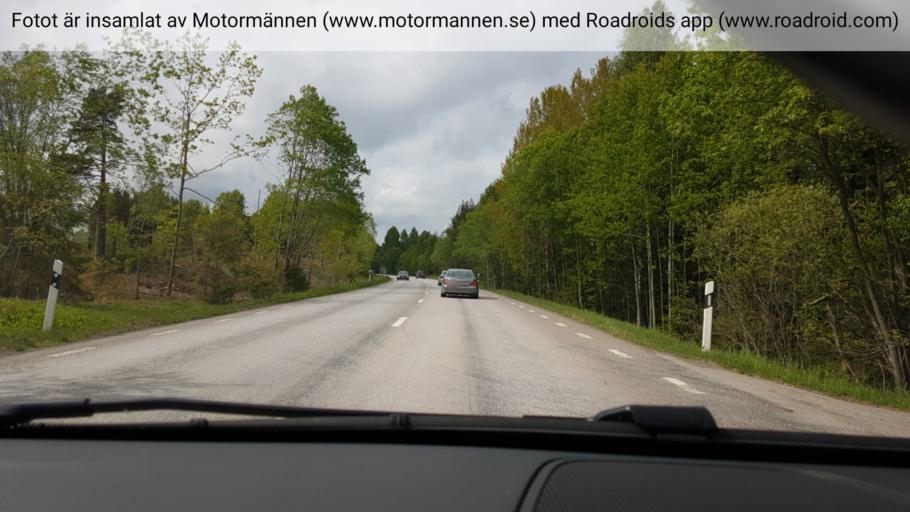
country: SE
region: Uppsala
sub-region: Osthammars Kommun
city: Osterbybruk
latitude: 60.1792
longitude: 17.9146
